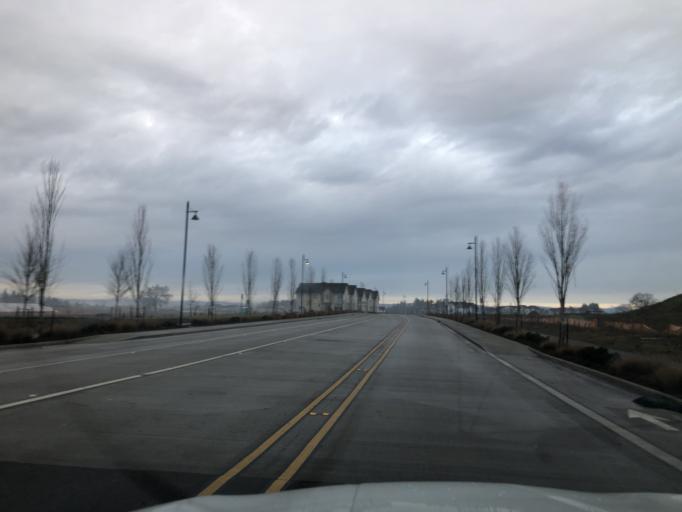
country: US
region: Oregon
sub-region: Washington County
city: Aloha
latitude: 45.4929
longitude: -122.9003
